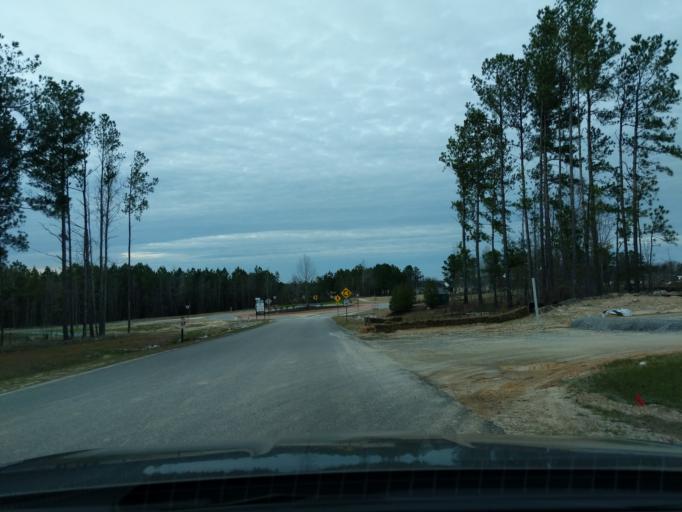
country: US
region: Georgia
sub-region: Columbia County
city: Grovetown
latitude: 33.4660
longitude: -82.1996
